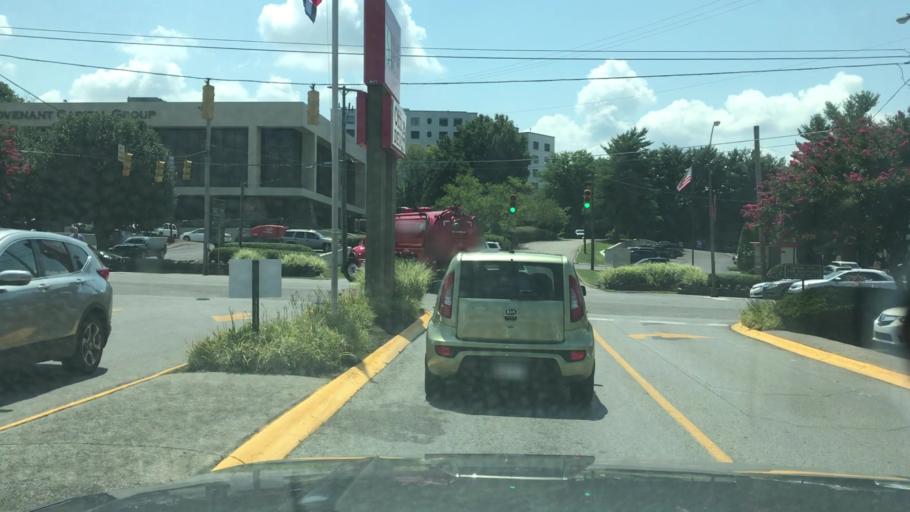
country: US
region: Tennessee
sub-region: Davidson County
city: Belle Meade
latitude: 36.1242
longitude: -86.8493
